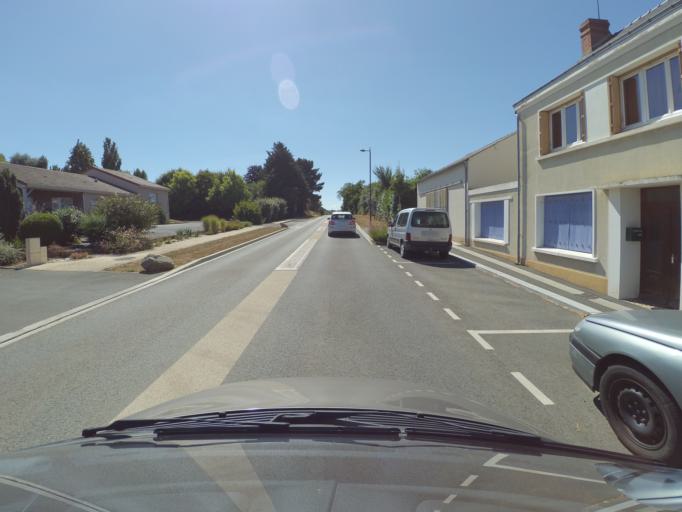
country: FR
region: Pays de la Loire
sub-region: Departement de Maine-et-Loire
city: Vihiers
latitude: 47.1446
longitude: -0.5431
